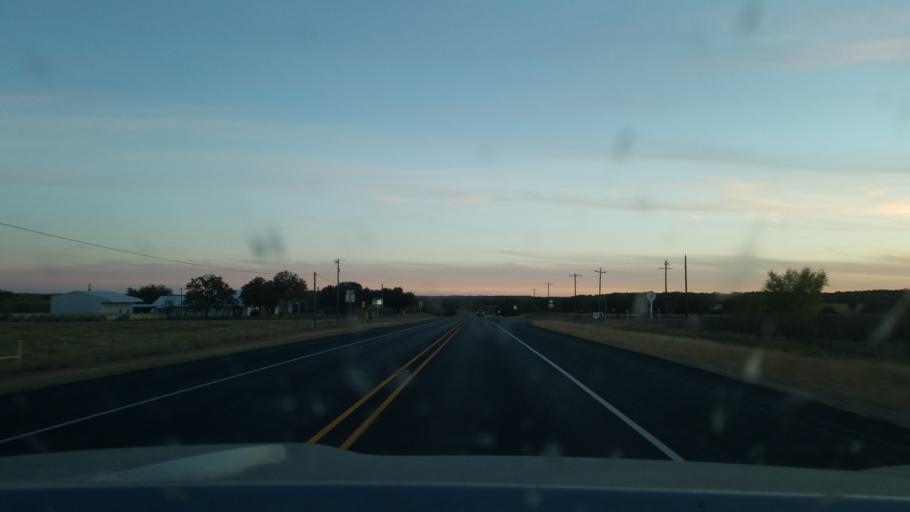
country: US
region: Texas
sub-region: Stephens County
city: Breckenridge
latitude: 32.6028
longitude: -98.8997
